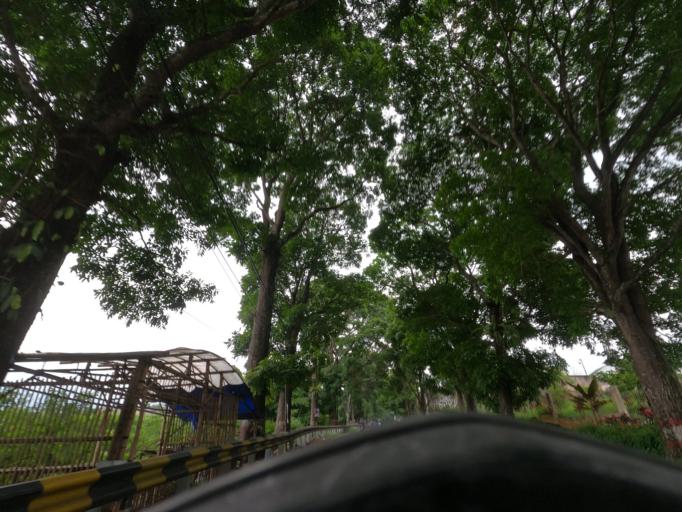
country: ID
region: West Java
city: Sukabumi
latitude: -6.7898
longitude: 107.0676
